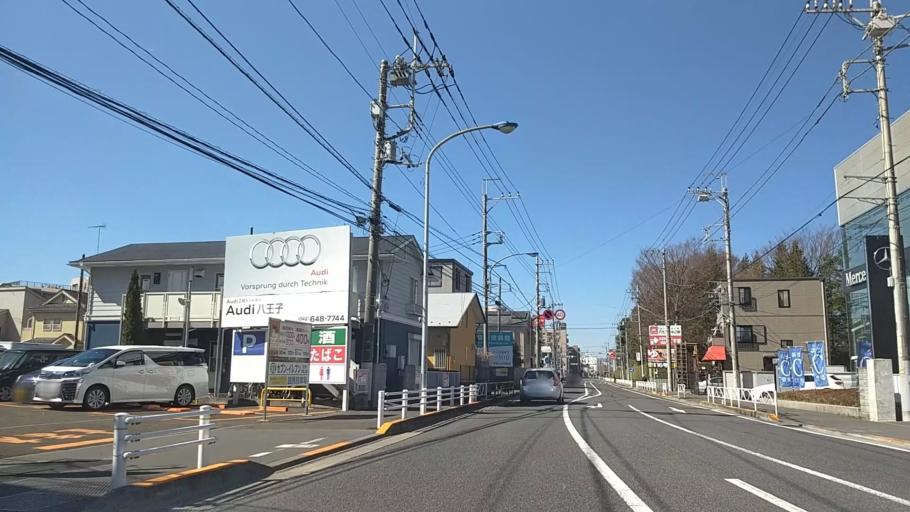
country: JP
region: Tokyo
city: Hino
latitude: 35.6741
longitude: 139.3850
